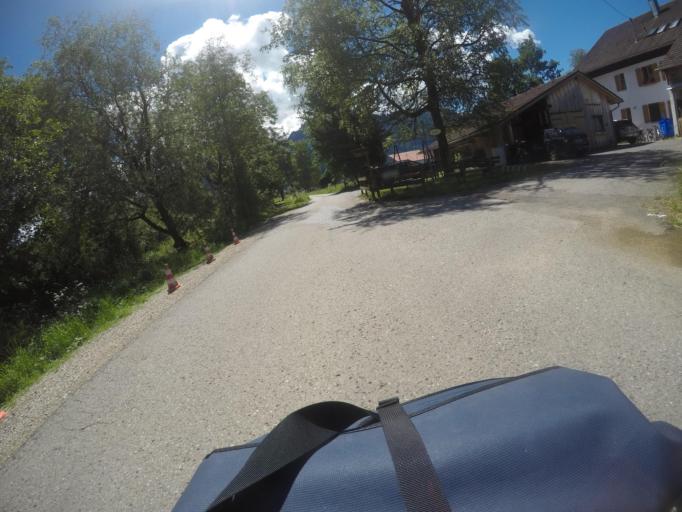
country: DE
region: Bavaria
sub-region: Swabia
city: Schwangau
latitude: 47.5909
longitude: 10.7444
